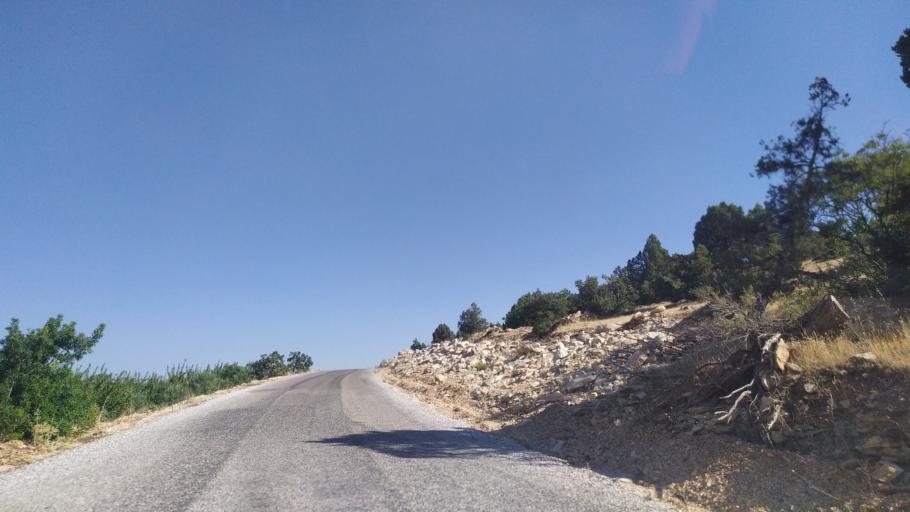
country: TR
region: Mersin
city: Mut
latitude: 36.6995
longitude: 33.4801
